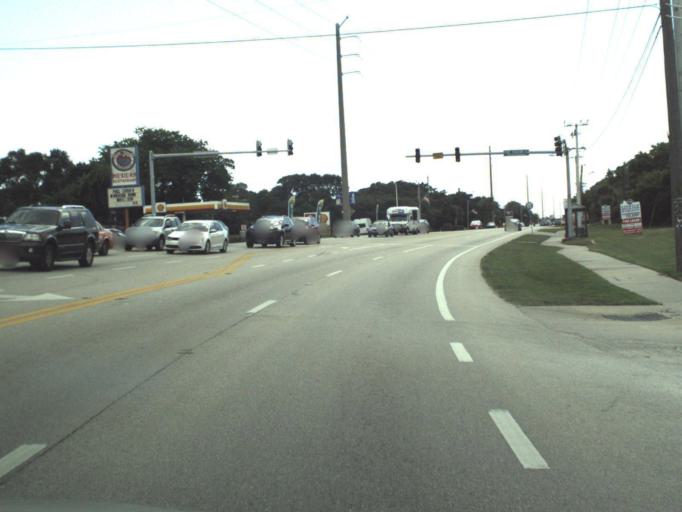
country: US
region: Florida
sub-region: Brevard County
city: Cape Canaveral
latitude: 28.3877
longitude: -80.6058
